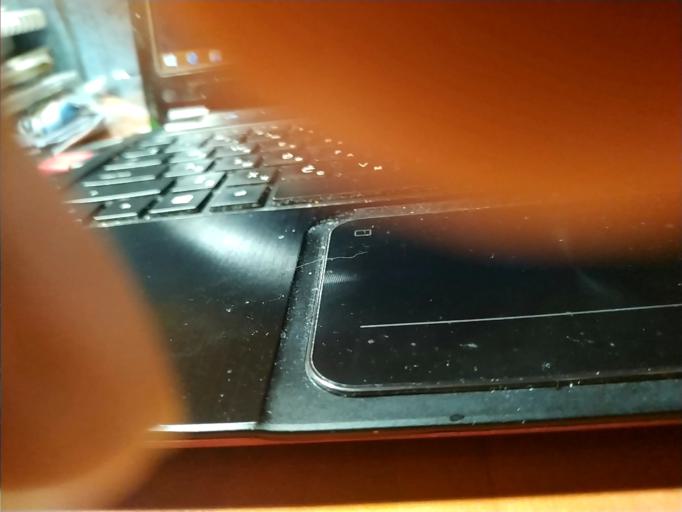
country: RU
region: Tverskaya
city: Ves'yegonsk
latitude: 58.7027
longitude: 37.5439
